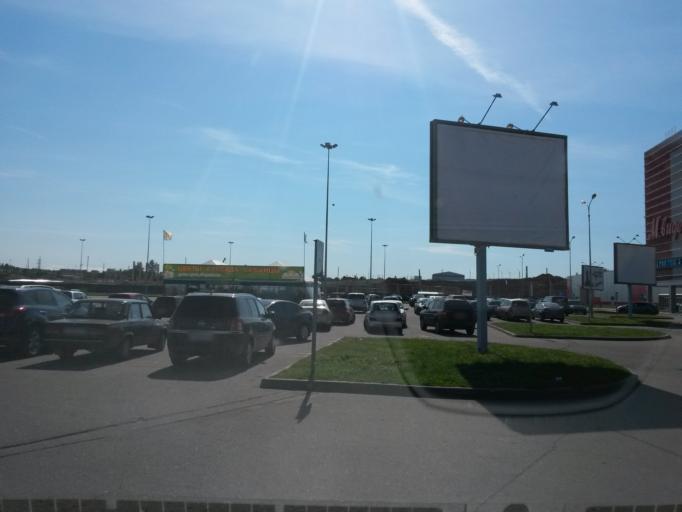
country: RU
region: Jaroslavl
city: Yaroslavl
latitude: 57.5706
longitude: 39.8436
